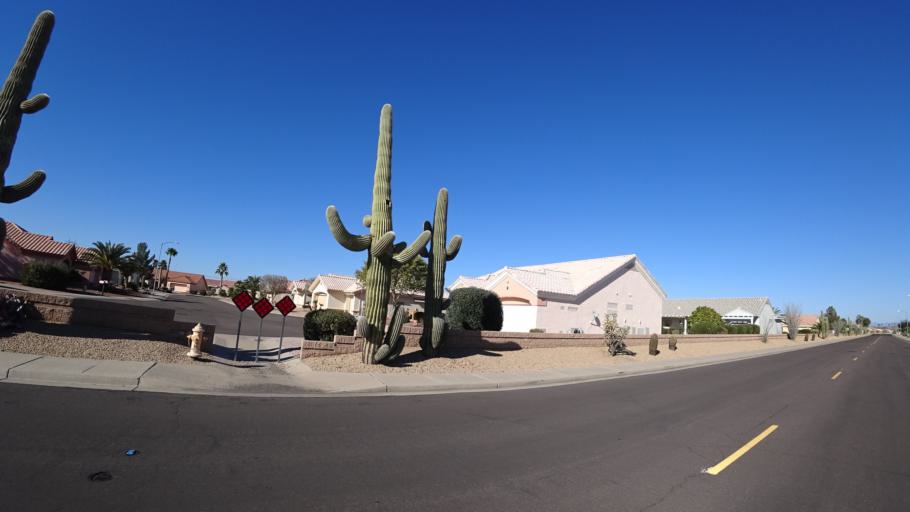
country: US
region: Arizona
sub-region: Maricopa County
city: Sun City West
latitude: 33.6916
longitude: -112.3805
